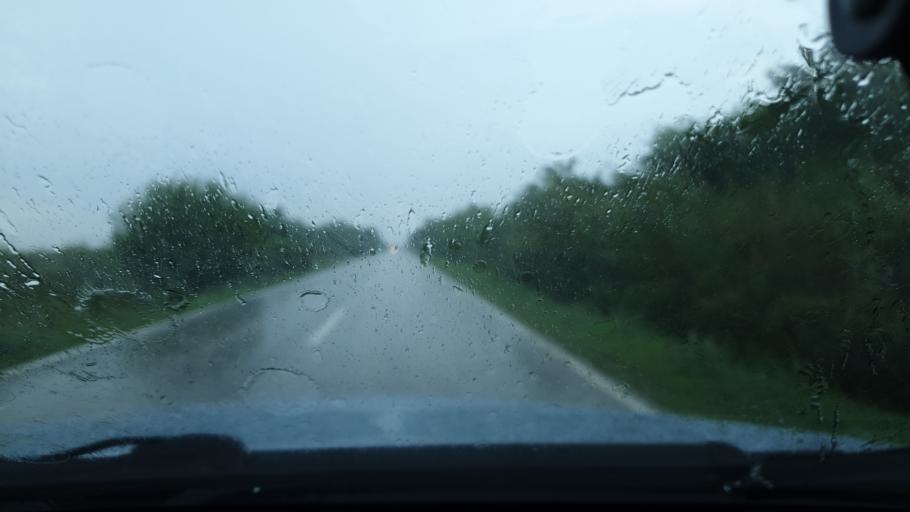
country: RS
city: Lazarevo
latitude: 45.3889
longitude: 20.5937
